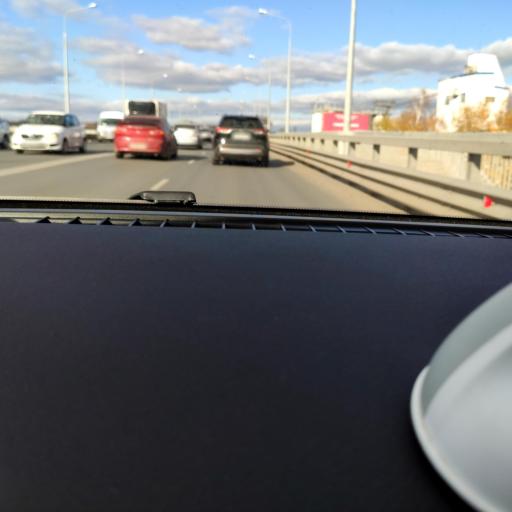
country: RU
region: Samara
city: Samara
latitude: 53.1739
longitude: 50.1943
